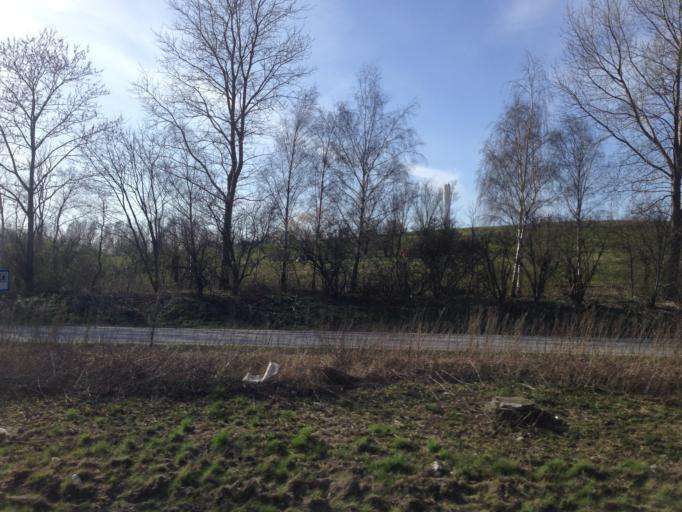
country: SE
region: Skane
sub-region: Burlovs Kommun
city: Arloev
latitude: 55.6289
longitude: 13.0542
